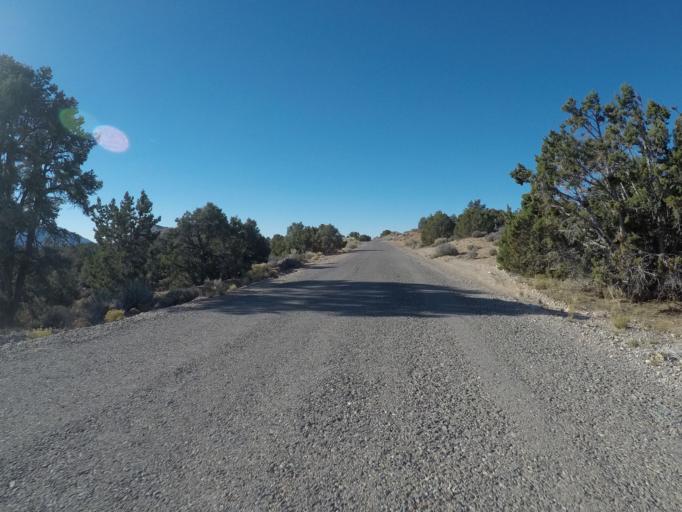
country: US
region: Nevada
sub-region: Clark County
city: Summerlin South
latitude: 36.0786
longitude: -115.5643
